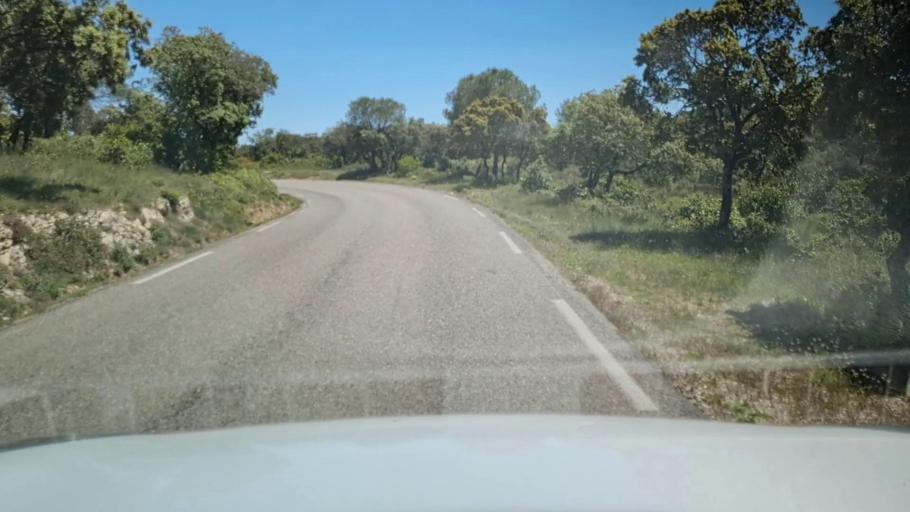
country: FR
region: Languedoc-Roussillon
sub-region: Departement du Gard
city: Clarensac
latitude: 43.8441
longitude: 4.2288
